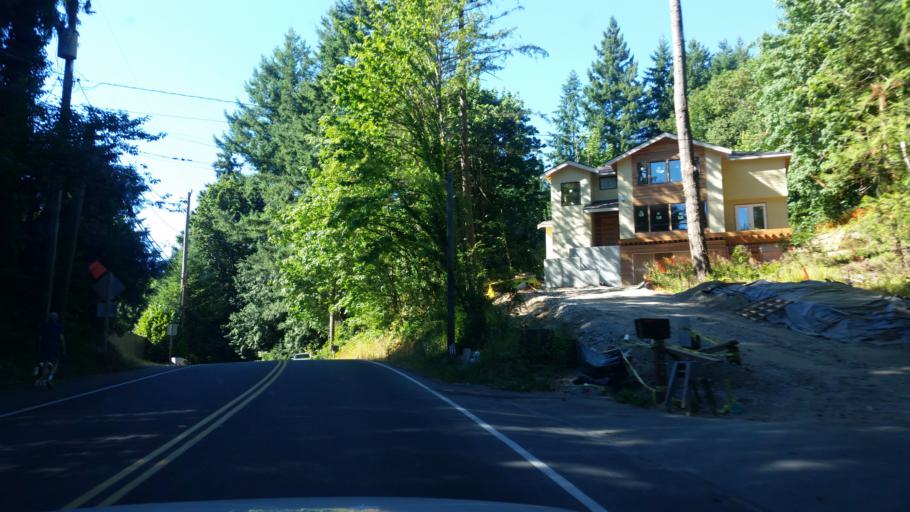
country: US
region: Washington
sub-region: King County
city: Lake Forest Park
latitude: 47.7678
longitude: -122.2839
